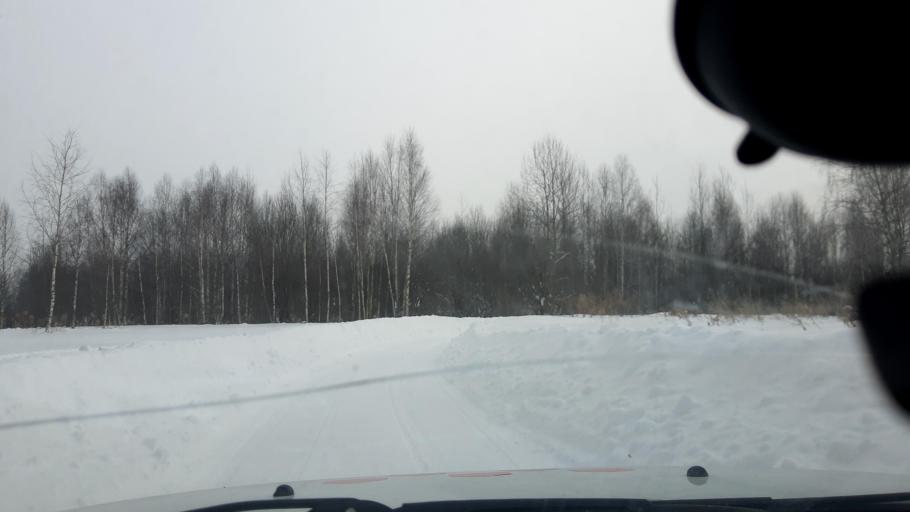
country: RU
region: Nizjnij Novgorod
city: Lukino
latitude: 56.5332
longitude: 43.7703
